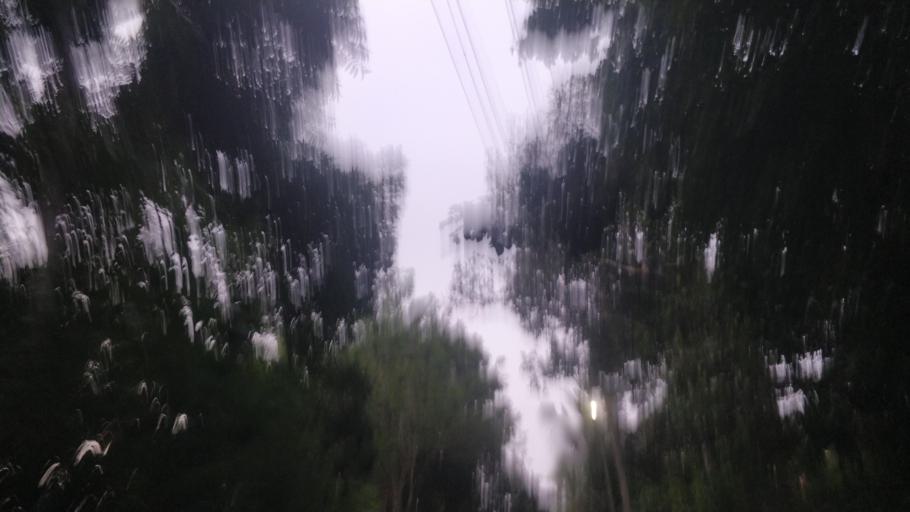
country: IN
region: Kerala
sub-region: Alappuzha
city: Shertallai
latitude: 9.6457
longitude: 76.3282
